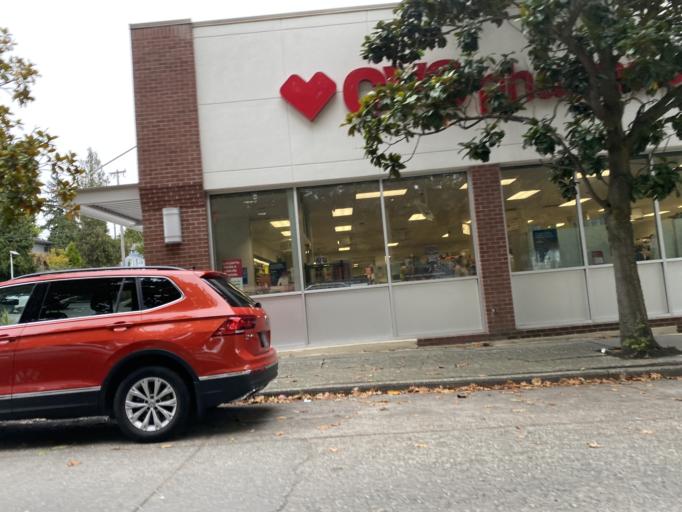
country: US
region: Washington
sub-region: King County
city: Seattle
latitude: 47.6409
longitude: -122.3984
